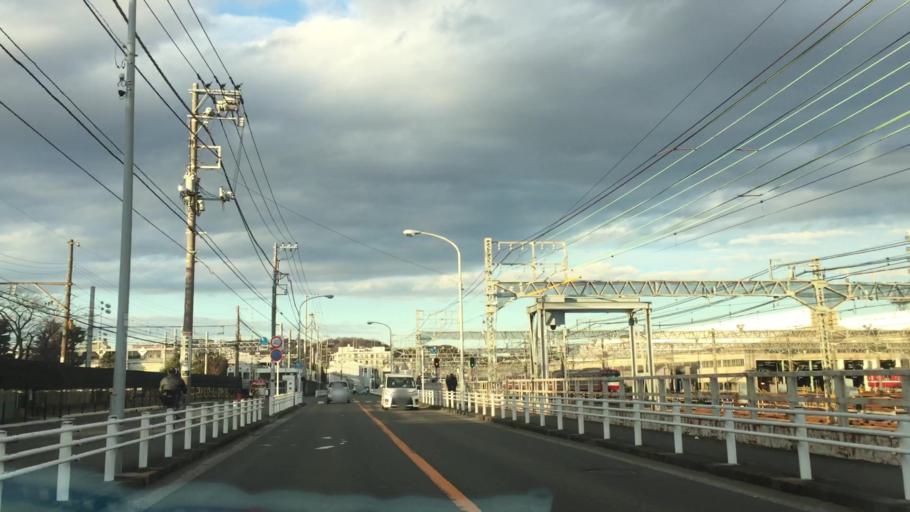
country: JP
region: Kanagawa
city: Zushi
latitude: 35.3348
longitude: 139.6199
